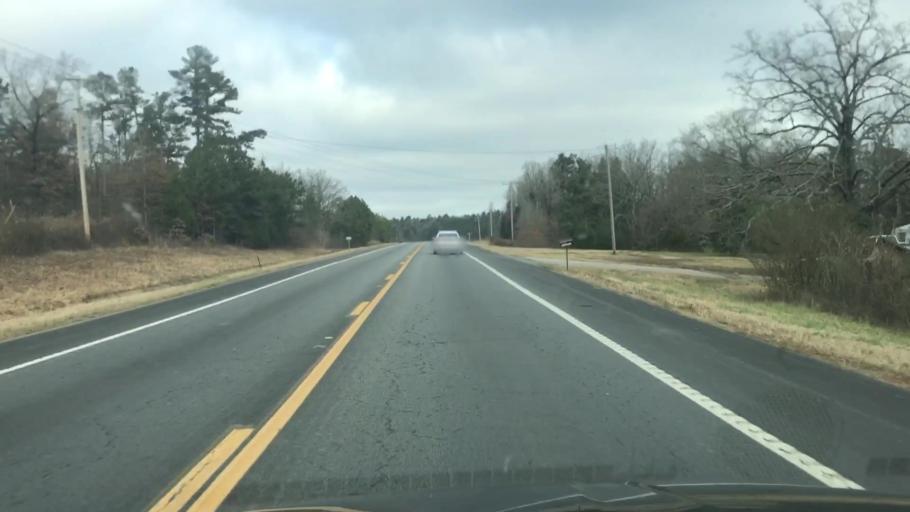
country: US
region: Arkansas
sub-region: Scott County
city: Waldron
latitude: 34.8327
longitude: -94.0427
